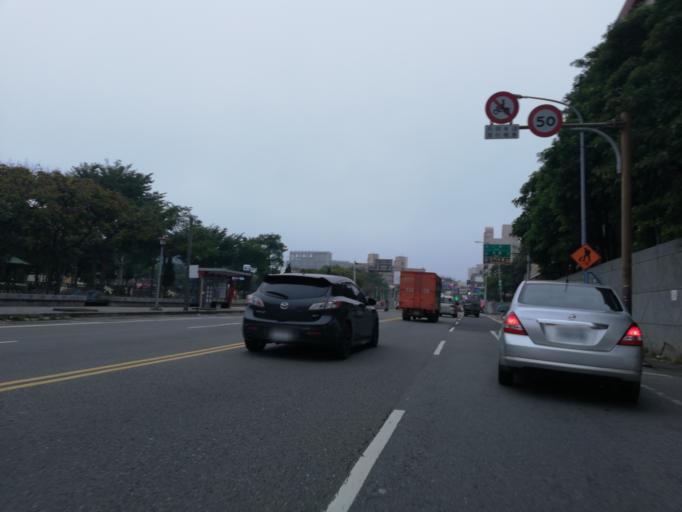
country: TW
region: Taiwan
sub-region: Taoyuan
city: Taoyuan
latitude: 24.9812
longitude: 121.3066
